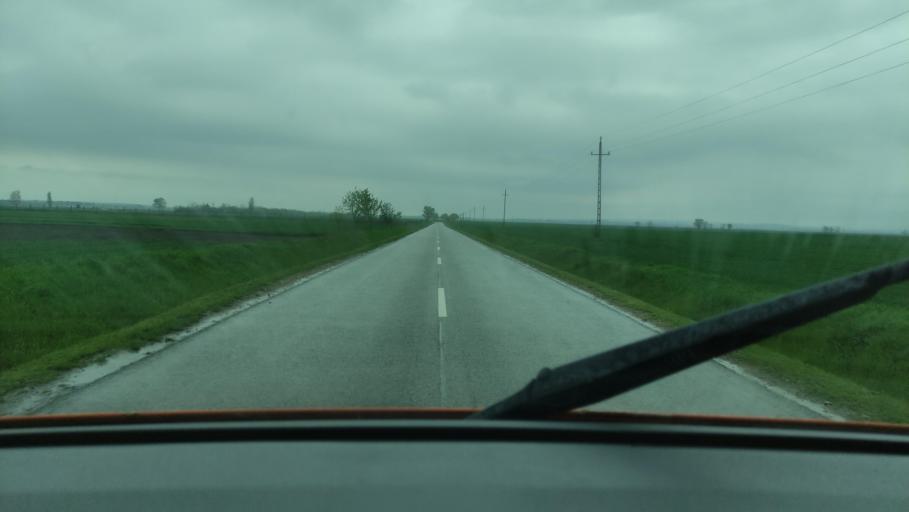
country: HU
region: Baranya
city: Mohacs
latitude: 45.9504
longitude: 18.6756
